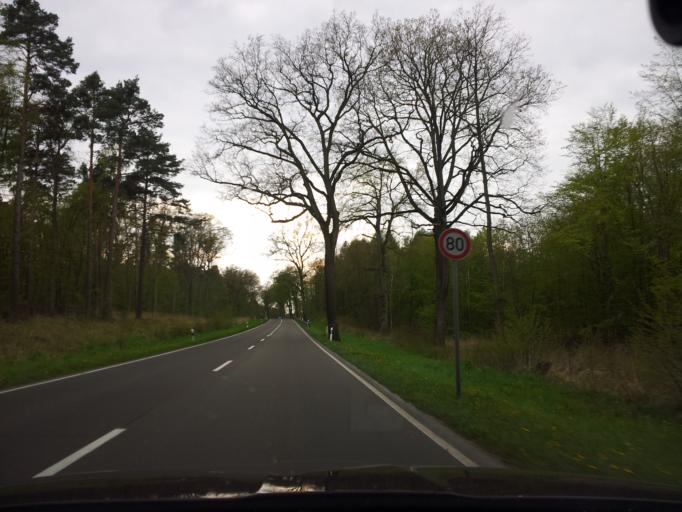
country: DE
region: Brandenburg
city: Rehfelde
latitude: 52.4819
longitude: 13.9869
